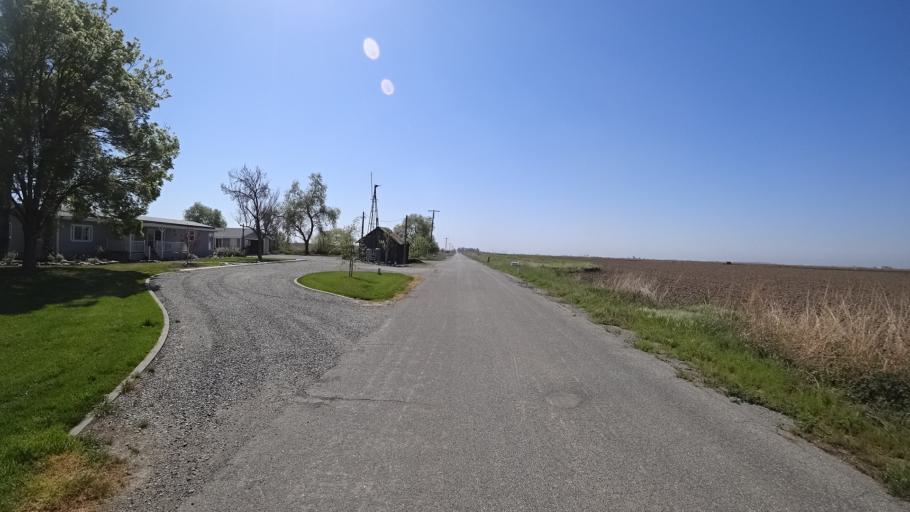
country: US
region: California
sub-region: Glenn County
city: Willows
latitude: 39.5123
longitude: -122.0373
